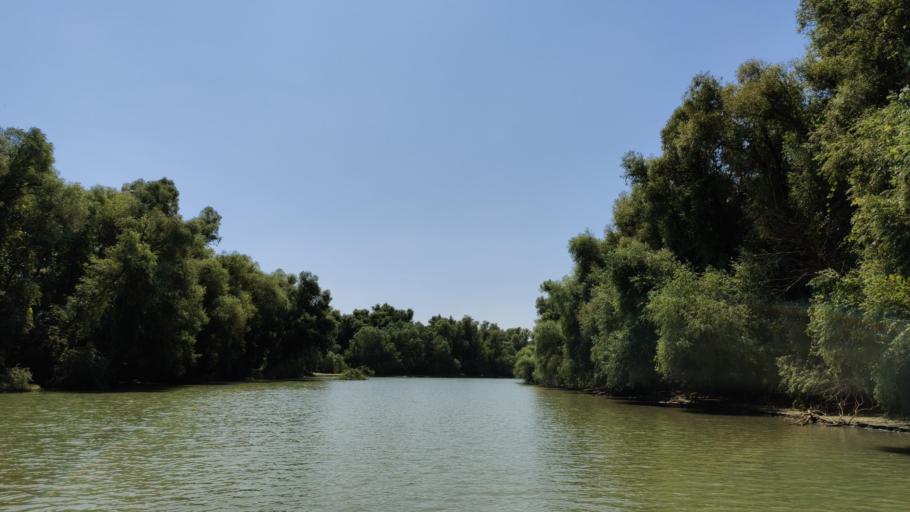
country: RO
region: Tulcea
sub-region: Comuna Pardina
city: Pardina
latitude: 45.2380
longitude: 28.9178
